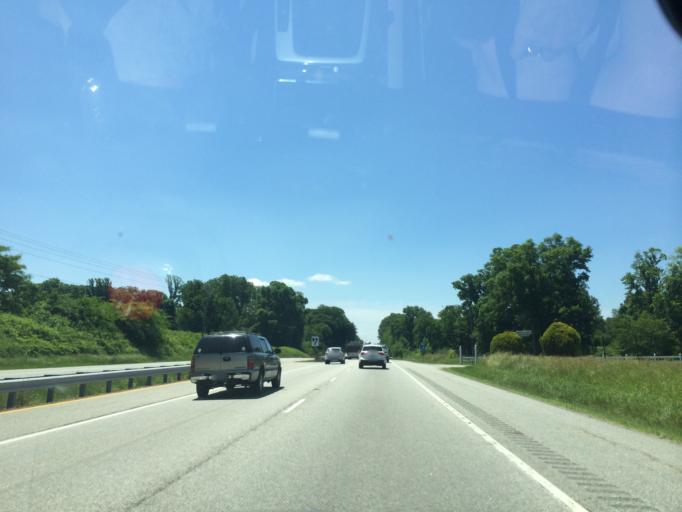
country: US
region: Maryland
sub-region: Talbot County
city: Easton
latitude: 38.8854
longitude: -76.0615
